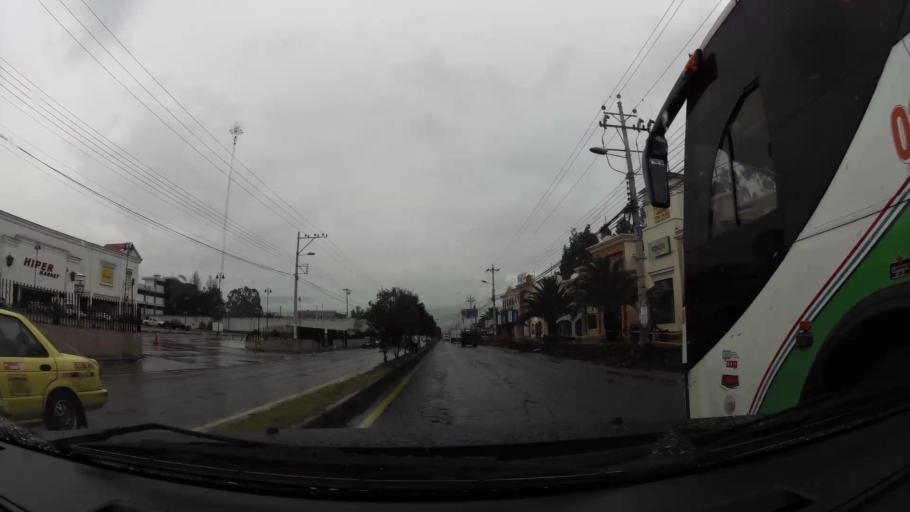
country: EC
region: Pichincha
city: Sangolqui
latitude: -0.3099
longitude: -78.4436
